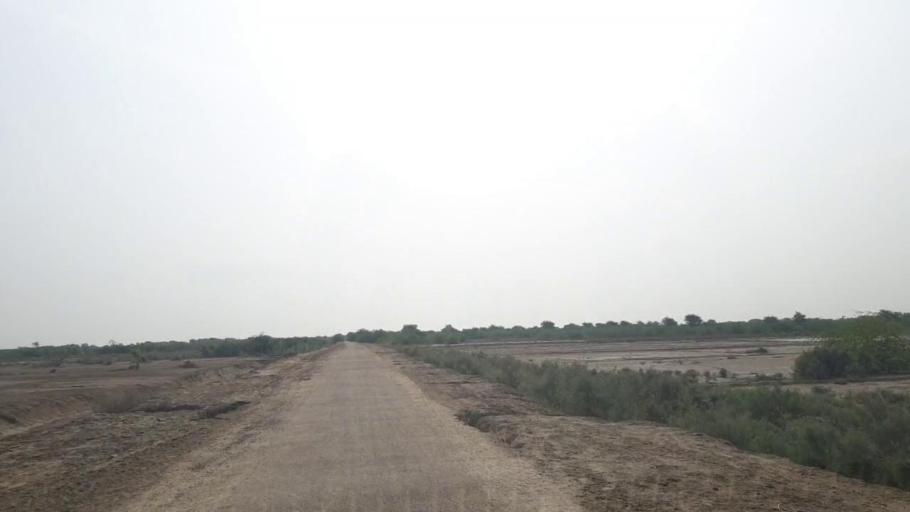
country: PK
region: Sindh
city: Badin
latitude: 24.5530
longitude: 68.6878
